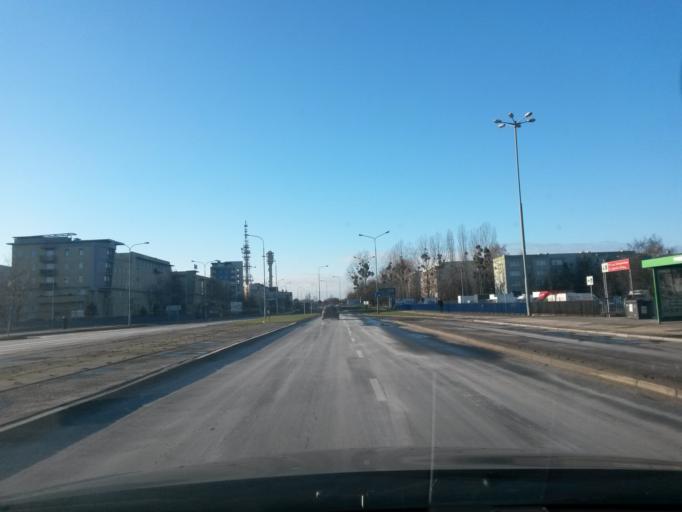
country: PL
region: Greater Poland Voivodeship
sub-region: Powiat poznanski
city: Suchy Las
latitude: 52.4605
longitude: 16.9173
